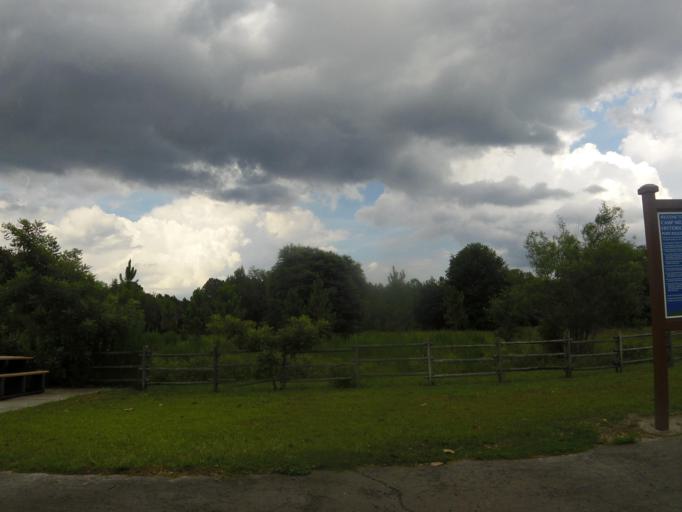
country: US
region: Florida
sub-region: Duval County
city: Baldwin
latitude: 30.3344
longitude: -81.8683
